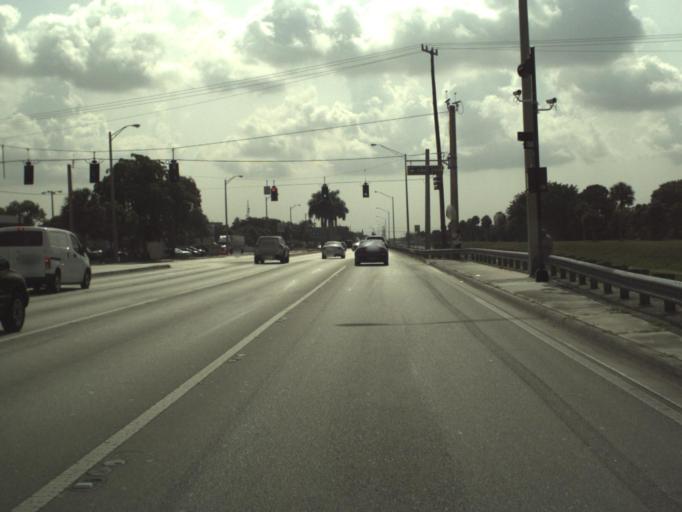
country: US
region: Florida
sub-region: Broward County
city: Plantation
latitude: 26.1357
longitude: -80.2322
